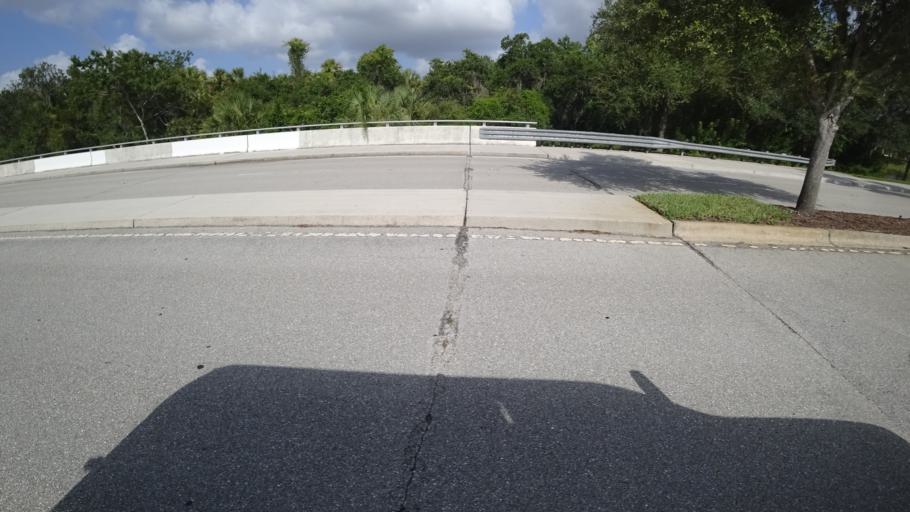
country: US
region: Florida
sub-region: Sarasota County
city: The Meadows
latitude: 27.4066
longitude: -82.4503
